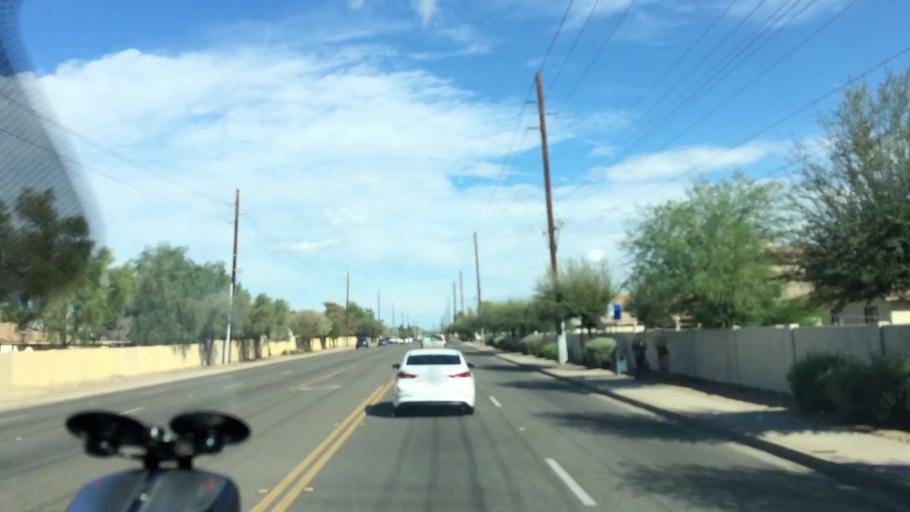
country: US
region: Arizona
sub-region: Maricopa County
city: Glendale
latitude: 33.5672
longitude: -112.1988
